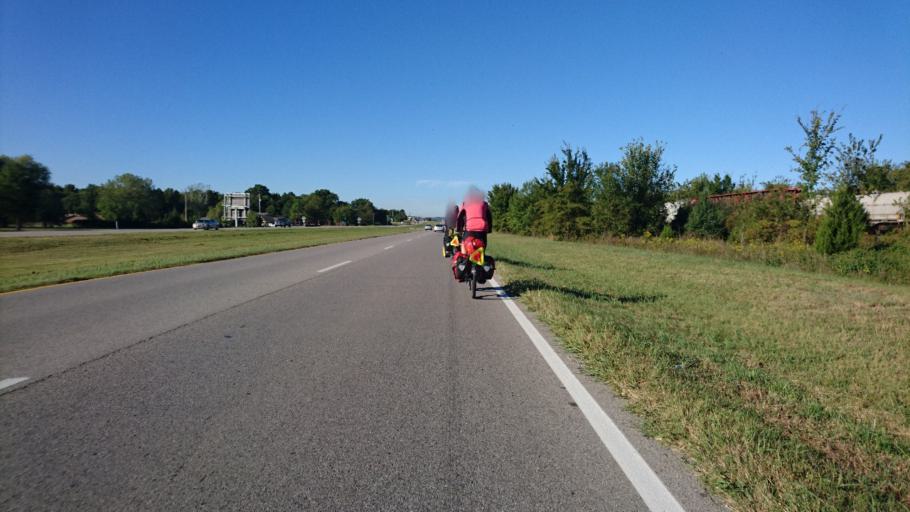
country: US
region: Oklahoma
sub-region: Rogers County
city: Verdigris
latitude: 36.2409
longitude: -95.6794
